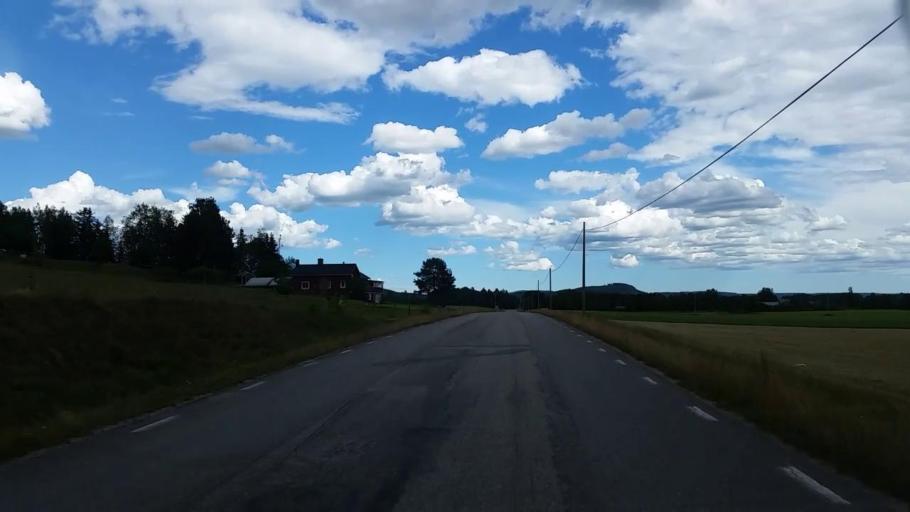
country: SE
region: Gaevleborg
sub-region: Ljusdals Kommun
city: Jaervsoe
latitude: 61.6715
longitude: 16.1034
